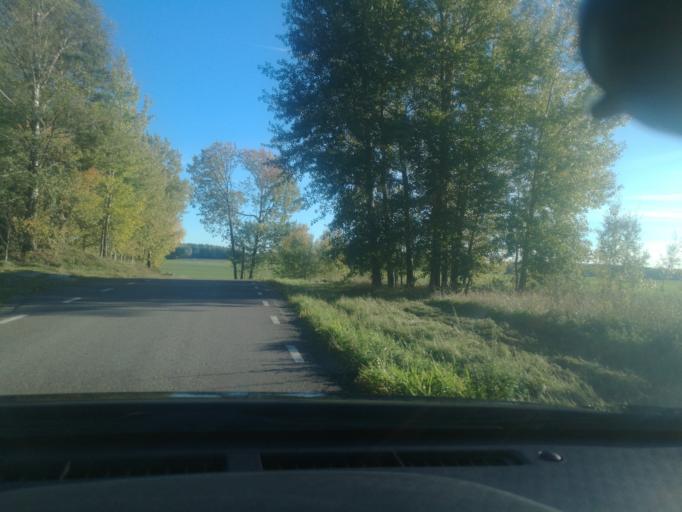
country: SE
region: Vaestmanland
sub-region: Kopings Kommun
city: Koping
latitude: 59.5708
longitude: 16.0249
